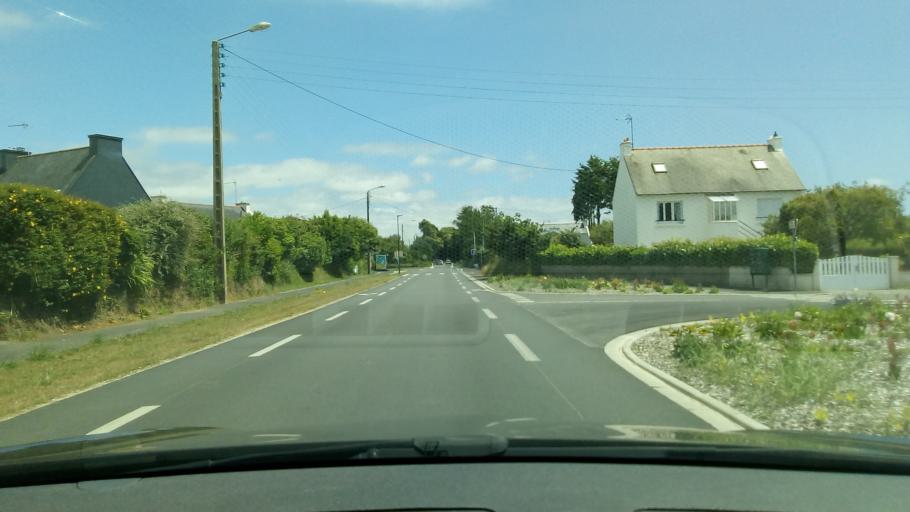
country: FR
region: Brittany
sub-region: Departement du Finistere
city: Melgven
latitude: 47.8812
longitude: -3.8428
